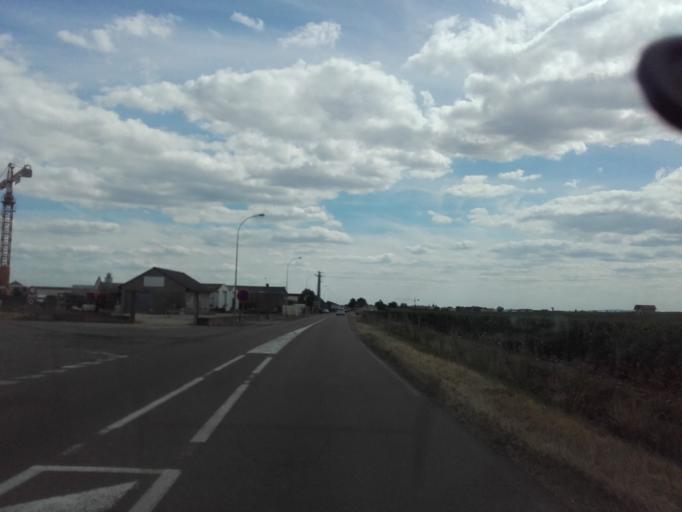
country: FR
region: Bourgogne
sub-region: Departement de la Cote-d'Or
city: Beaune
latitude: 47.0523
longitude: 4.8391
